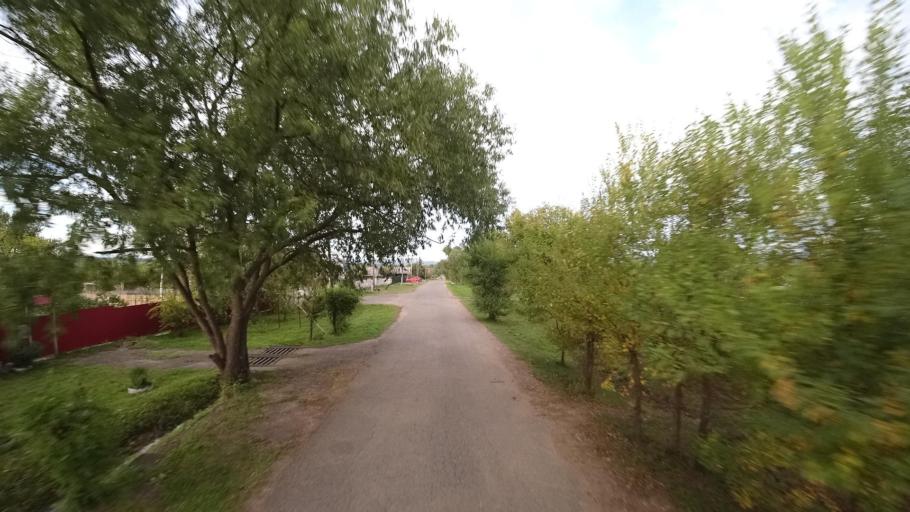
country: RU
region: Primorskiy
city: Yakovlevka
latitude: 44.4205
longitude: 133.4682
